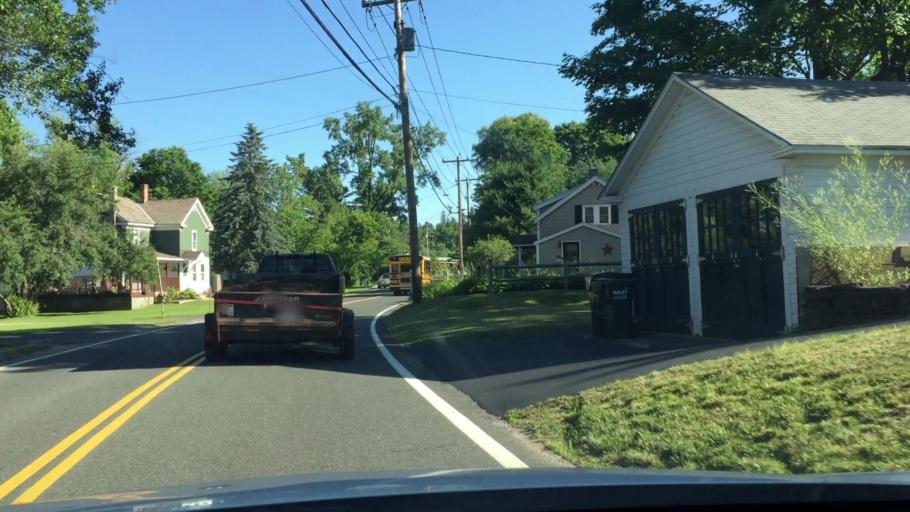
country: US
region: Massachusetts
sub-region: Berkshire County
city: Lee
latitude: 42.2937
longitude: -73.2389
